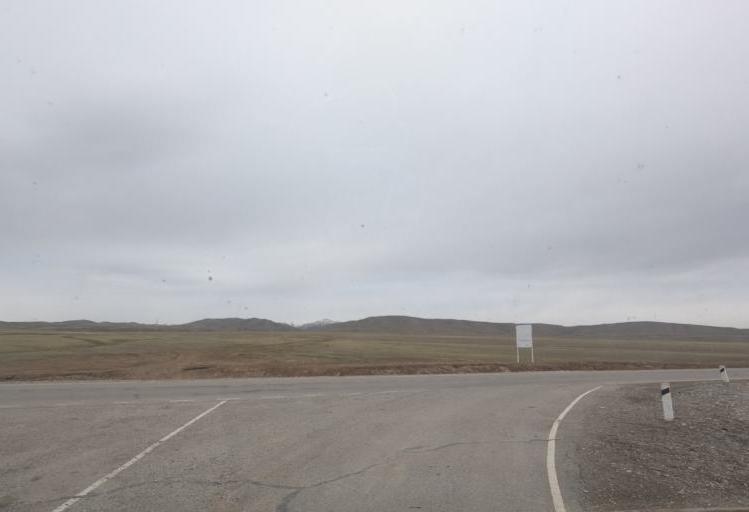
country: KG
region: Naryn
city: Baetov
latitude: 40.9422
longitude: 75.2732
